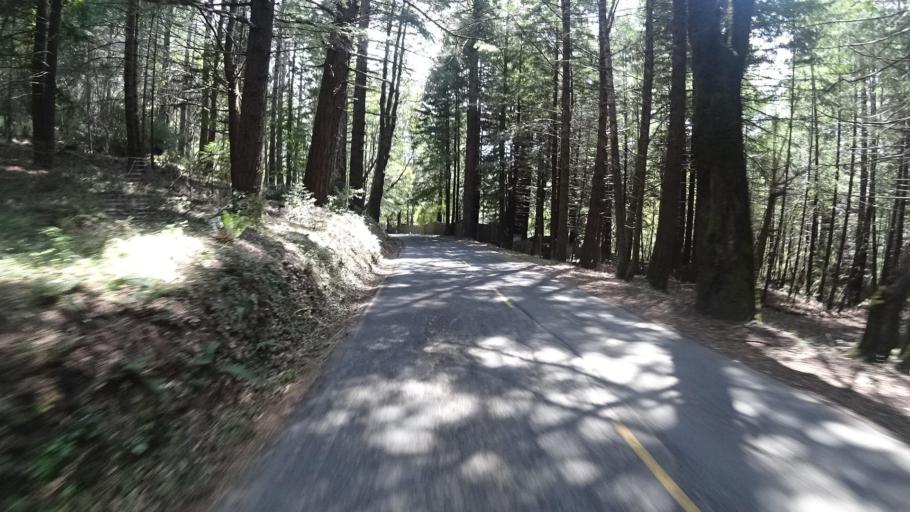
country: US
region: California
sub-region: Humboldt County
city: Redway
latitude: 40.0554
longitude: -123.9614
